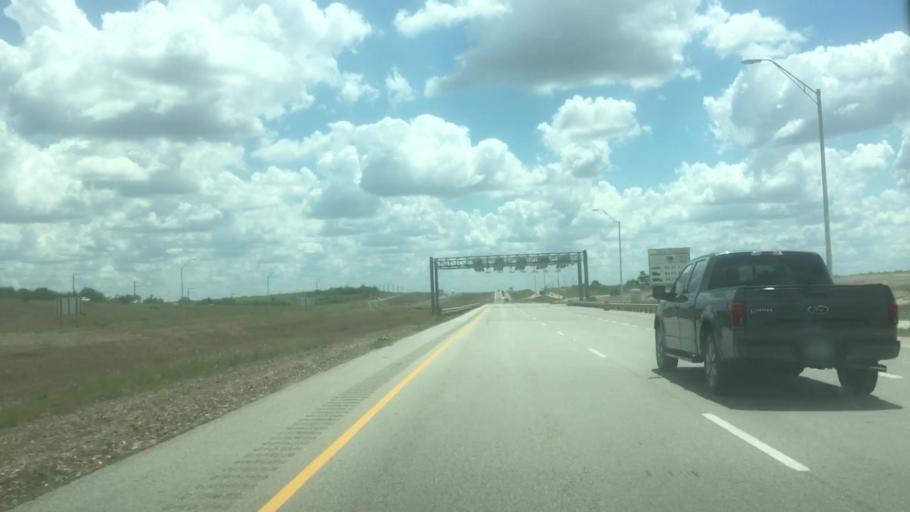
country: US
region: Texas
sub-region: Caldwell County
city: Lockhart
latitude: 29.9908
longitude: -97.6843
